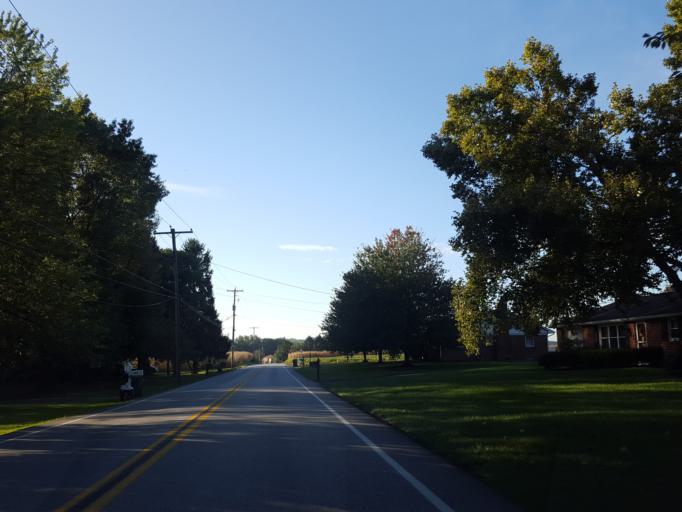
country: US
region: Pennsylvania
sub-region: York County
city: Stonybrook
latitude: 39.9700
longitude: -76.6149
